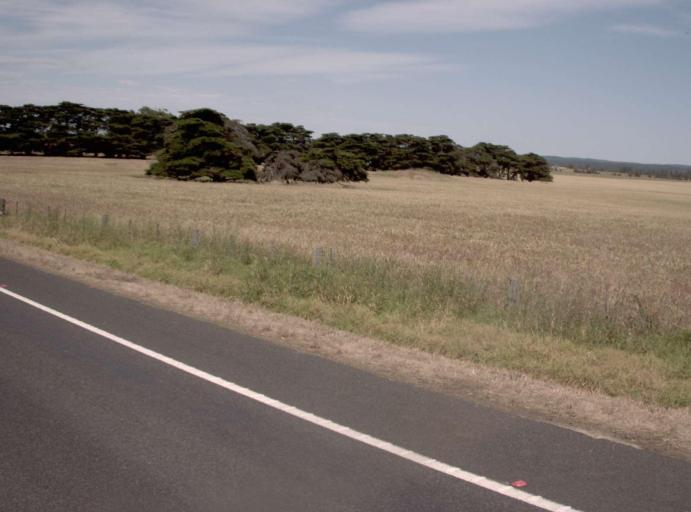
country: AU
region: Victoria
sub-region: Wellington
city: Heyfield
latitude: -38.1219
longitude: 146.8524
